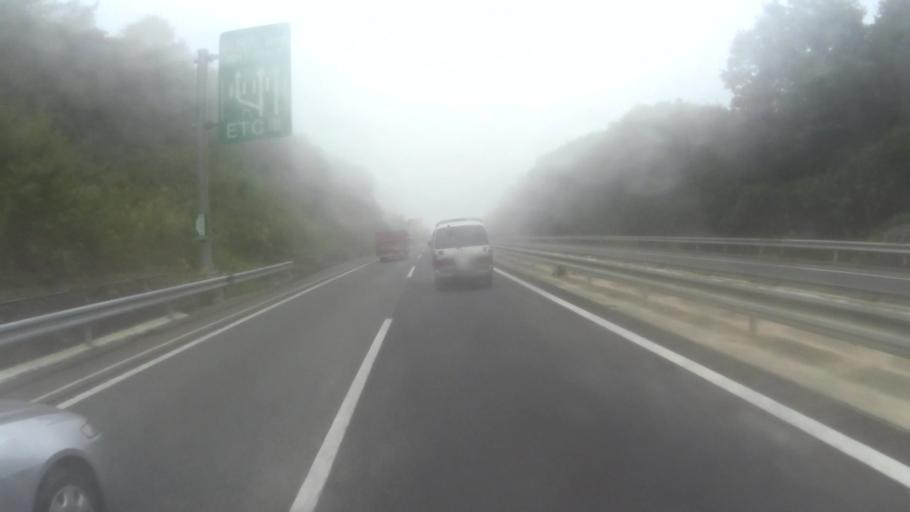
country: JP
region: Kyoto
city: Kameoka
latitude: 34.9902
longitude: 135.6173
